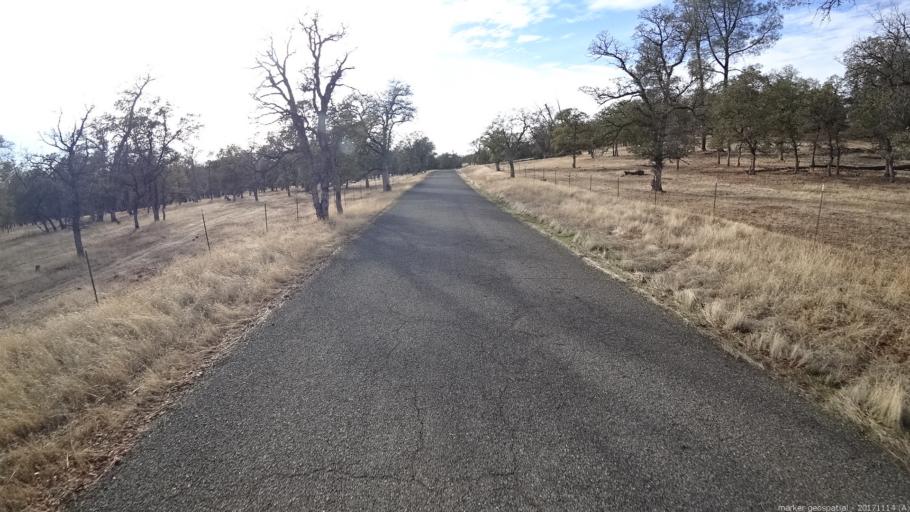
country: US
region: California
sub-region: Shasta County
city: Shasta
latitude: 40.3823
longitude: -122.5625
